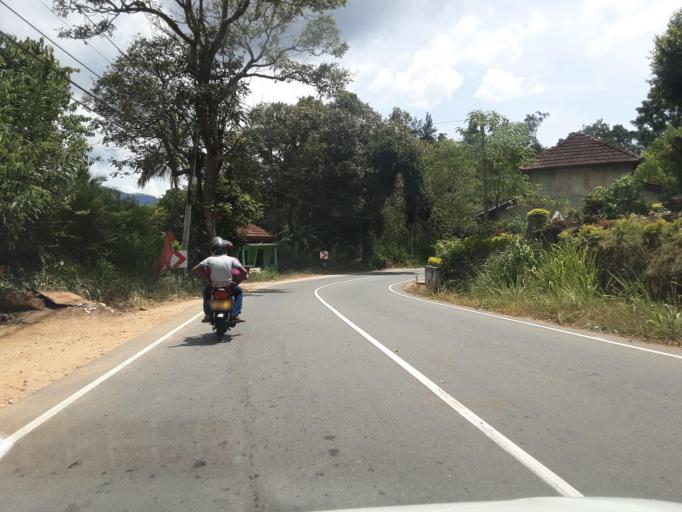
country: LK
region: Central
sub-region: Nuwara Eliya District
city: Nuwara Eliya
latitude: 6.9357
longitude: 80.9091
